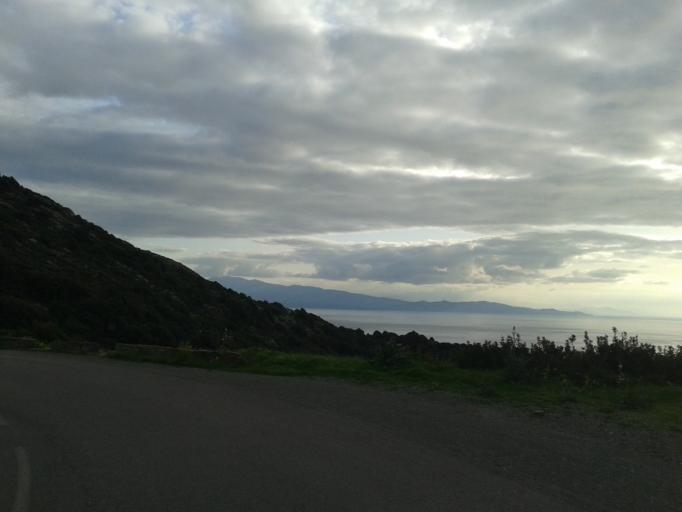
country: FR
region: Corsica
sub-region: Departement de la Haute-Corse
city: Brando
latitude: 42.8850
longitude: 9.3332
